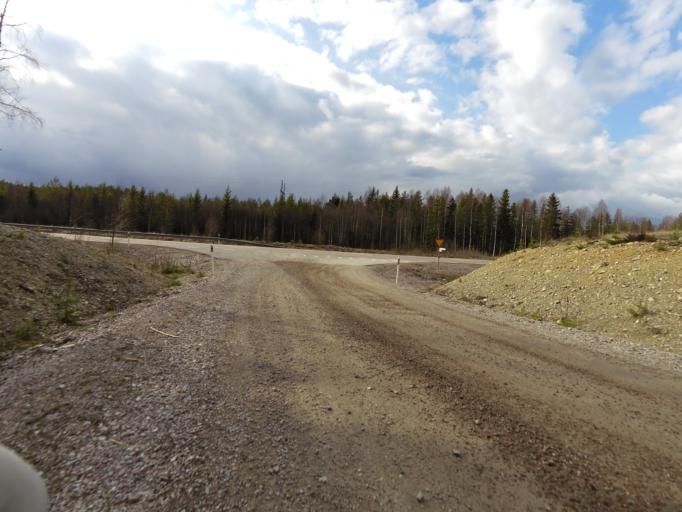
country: SE
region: Gaevleborg
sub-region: Hofors Kommun
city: Hofors
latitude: 60.4848
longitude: 16.4449
